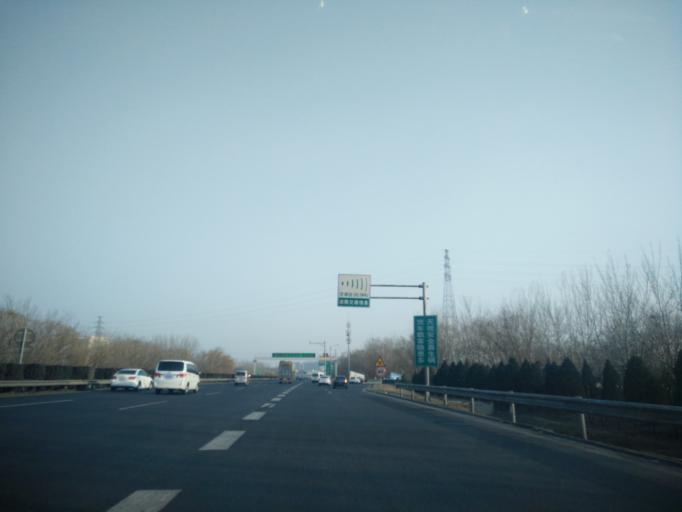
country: CN
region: Beijing
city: Jiugong
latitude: 39.8143
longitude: 116.5054
